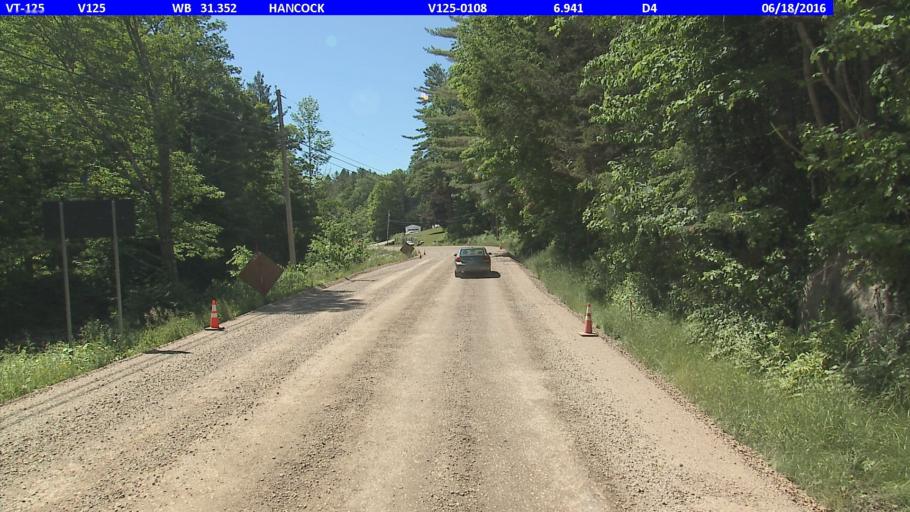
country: US
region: Vermont
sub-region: Orange County
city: Randolph
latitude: 43.9275
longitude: -72.8469
